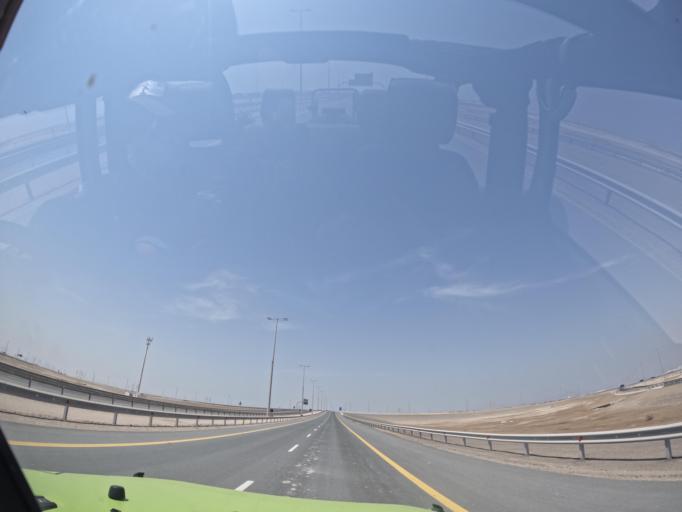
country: AE
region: Abu Dhabi
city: Abu Dhabi
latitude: 24.2433
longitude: 54.4771
